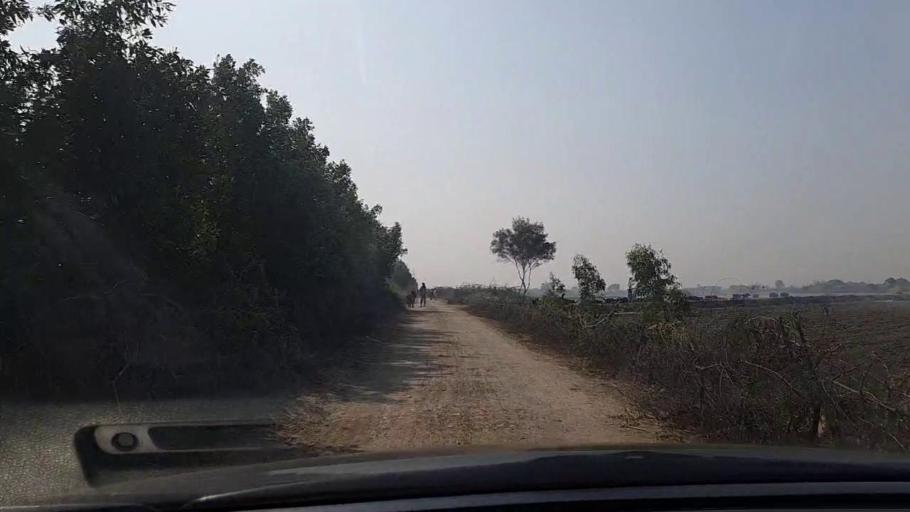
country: PK
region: Sindh
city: Mirpur Sakro
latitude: 24.5734
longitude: 67.7804
